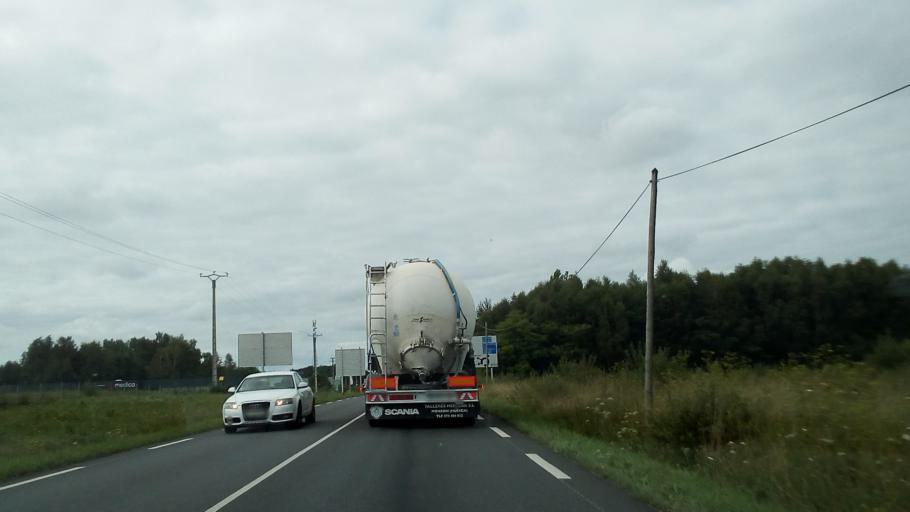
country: FR
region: Midi-Pyrenees
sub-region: Departement des Hautes-Pyrenees
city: La Barthe-de-Neste
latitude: 43.0939
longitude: 0.3901
